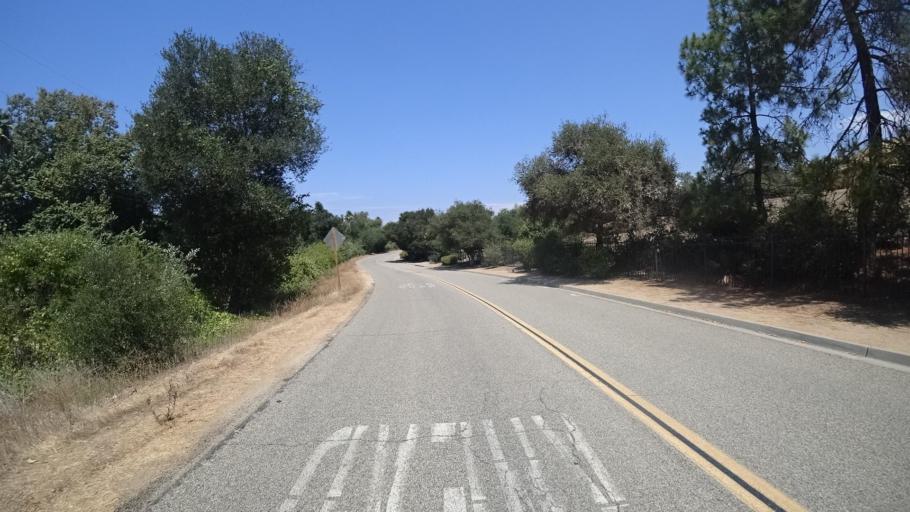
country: US
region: California
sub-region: San Diego County
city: Bonsall
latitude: 33.3181
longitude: -117.2172
